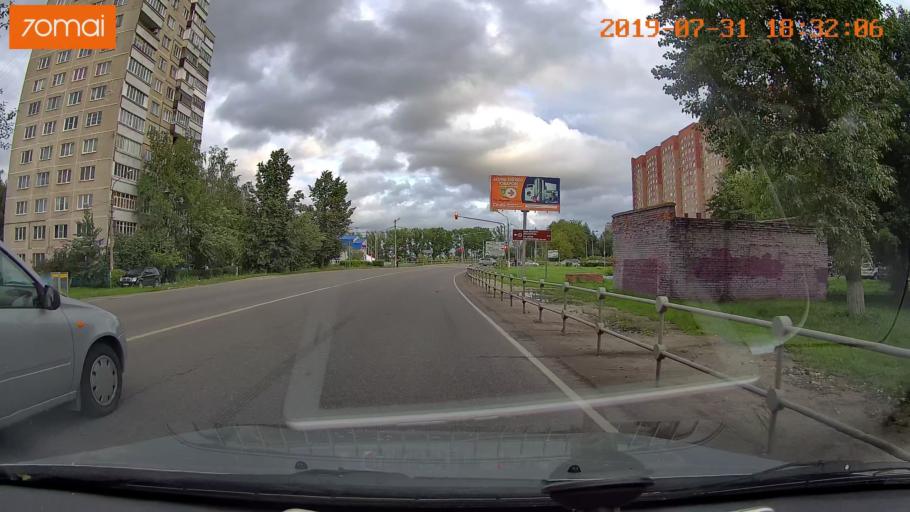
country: RU
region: Moskovskaya
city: Voskresensk
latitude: 55.3139
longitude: 38.6527
